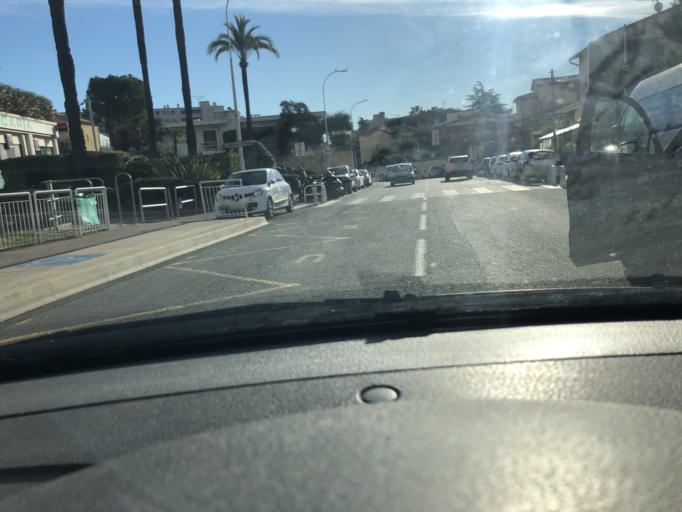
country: FR
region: Provence-Alpes-Cote d'Azur
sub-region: Departement des Alpes-Maritimes
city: Saint-Laurent-du-Var
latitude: 43.6782
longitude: 7.2201
